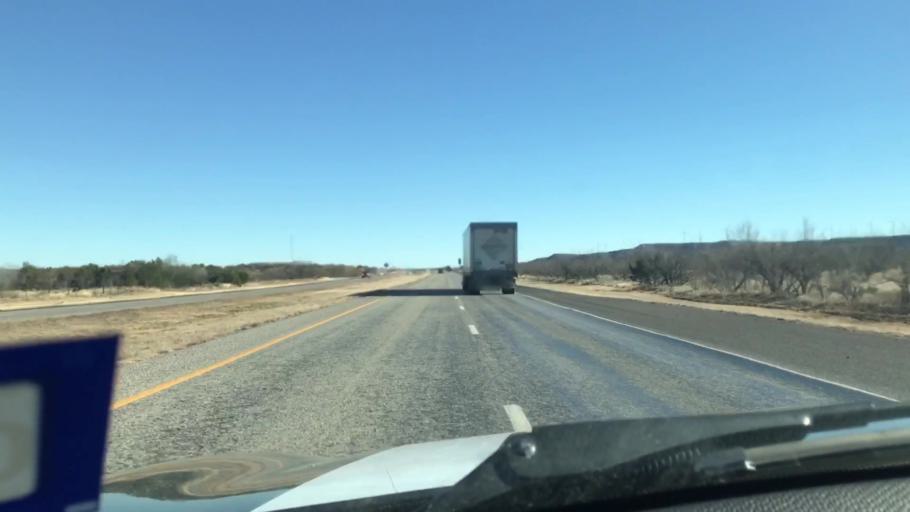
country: US
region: Texas
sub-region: Garza County
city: Post
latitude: 32.9951
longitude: -101.1497
